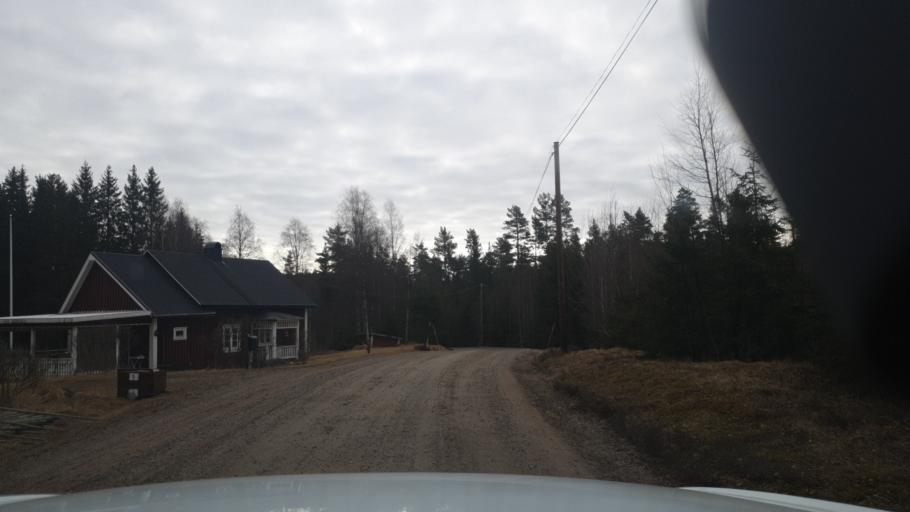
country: SE
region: Vaermland
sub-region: Arvika Kommun
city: Arvika
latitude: 59.8645
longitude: 12.6213
